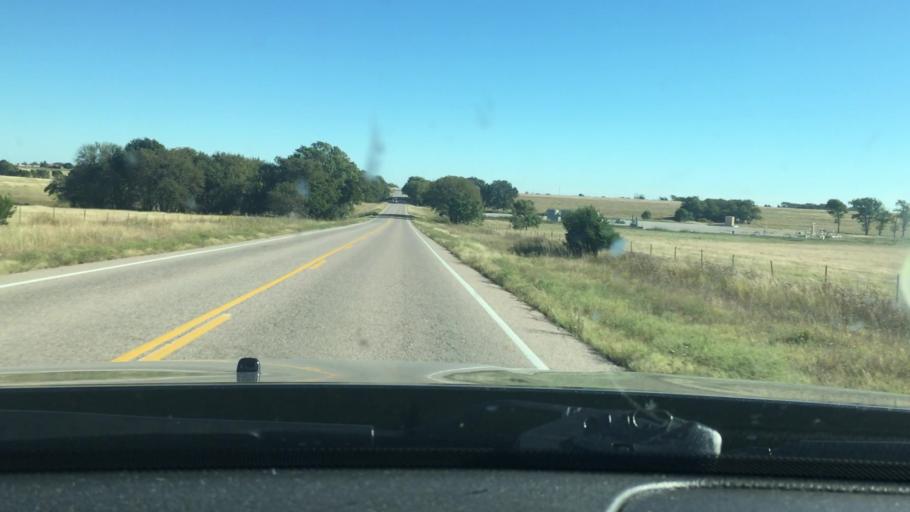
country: US
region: Oklahoma
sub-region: Marshall County
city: Madill
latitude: 34.1242
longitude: -96.7280
